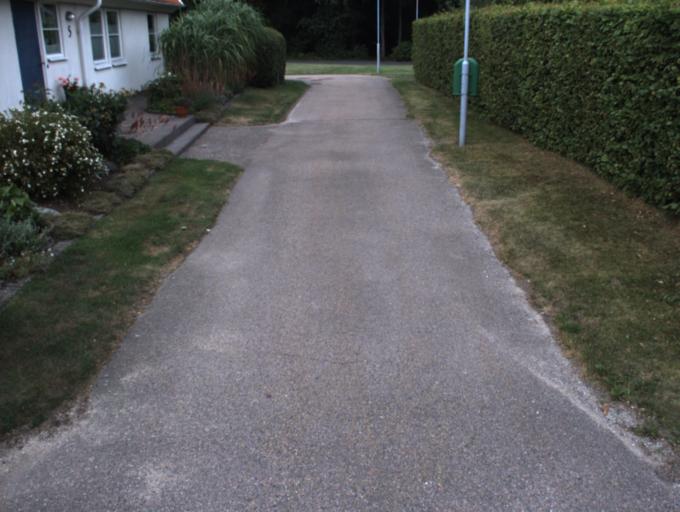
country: SE
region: Skane
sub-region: Helsingborg
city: Helsingborg
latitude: 56.0998
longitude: 12.6595
